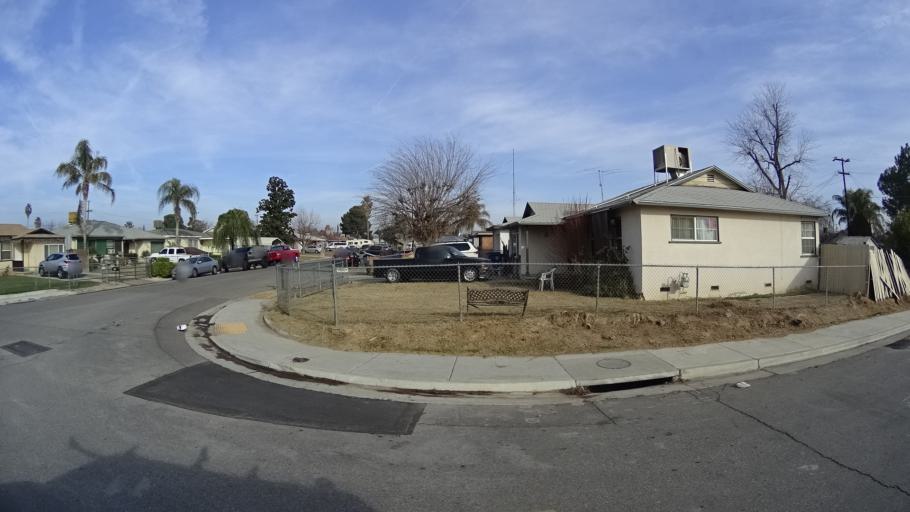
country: US
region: California
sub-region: Kern County
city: Bakersfield
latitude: 35.3615
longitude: -118.9539
